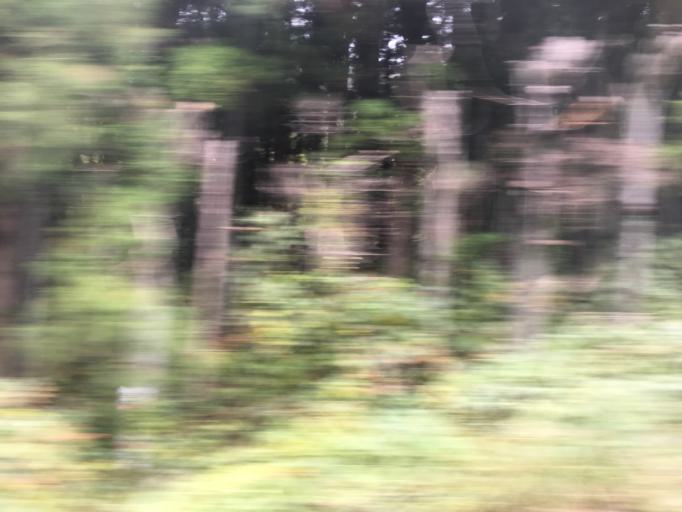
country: JP
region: Niigata
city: Murakami
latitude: 38.0800
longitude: 139.6532
